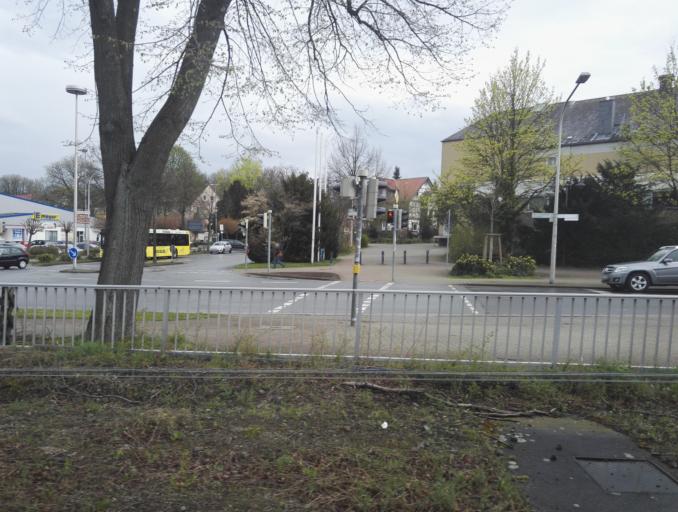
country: DE
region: Lower Saxony
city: Goslar
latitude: 51.9111
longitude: 10.4236
